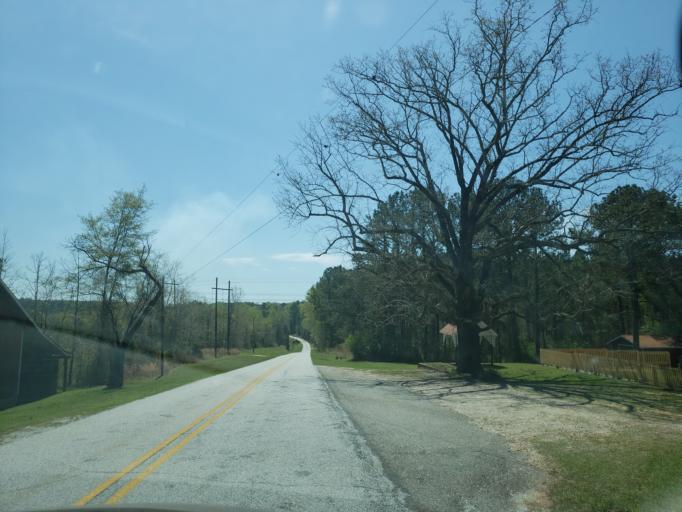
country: US
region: Alabama
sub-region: Elmore County
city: Tallassee
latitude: 32.6767
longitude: -85.8628
